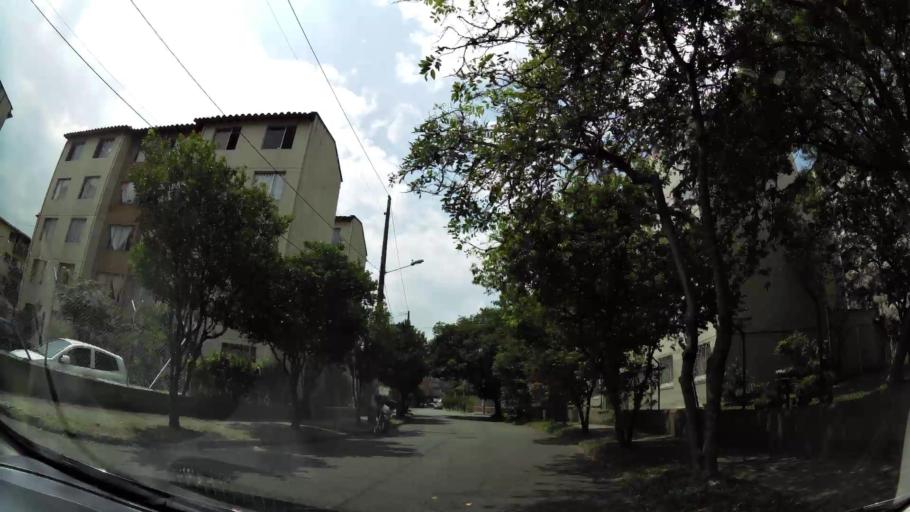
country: CO
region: Antioquia
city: Itagui
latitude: 6.1923
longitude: -75.5952
